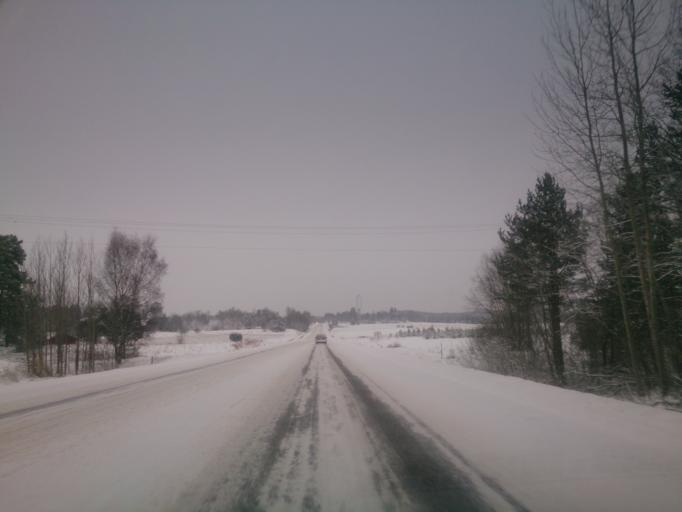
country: SE
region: OEstergoetland
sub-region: Norrkopings Kommun
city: Kimstad
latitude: 58.4954
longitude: 15.9587
